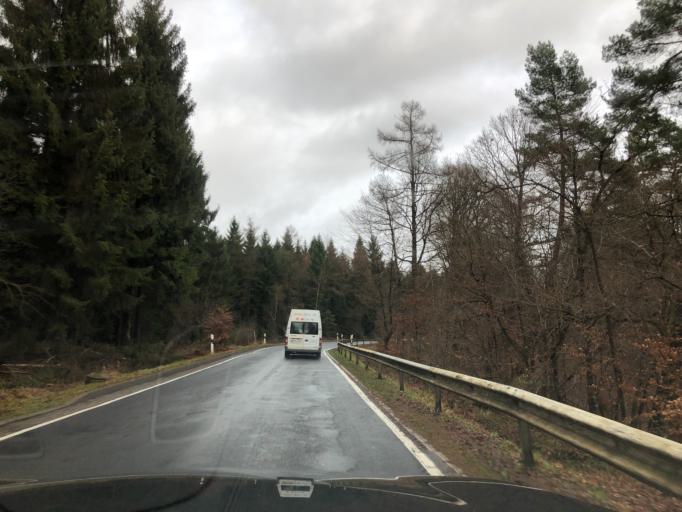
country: DE
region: Rheinland-Pfalz
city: Vettelschoss
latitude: 50.6172
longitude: 7.3026
